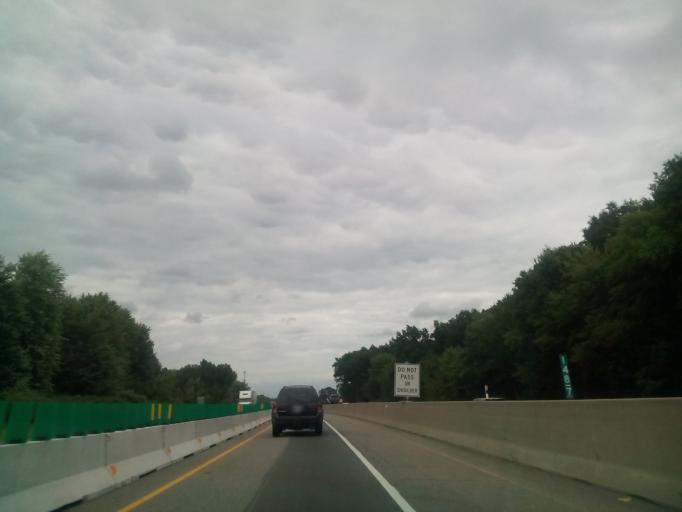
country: US
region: Ohio
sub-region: Lorain County
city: North Ridgeville
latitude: 41.3779
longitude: -82.0556
